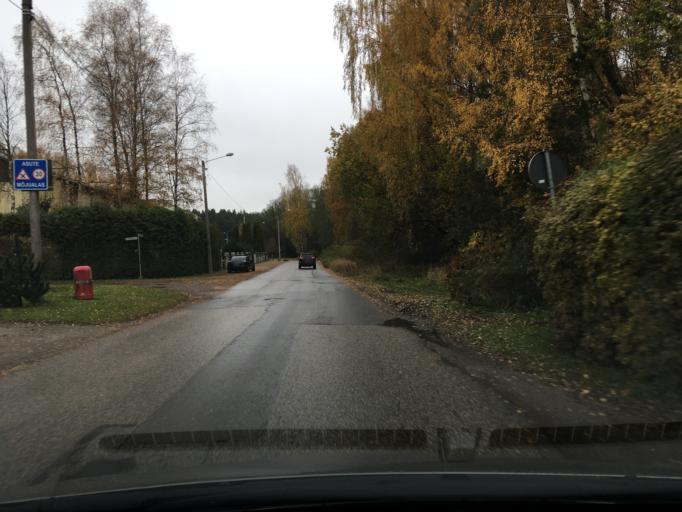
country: EE
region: Tartu
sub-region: Tartu linn
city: Tartu
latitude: 58.3577
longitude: 26.7790
